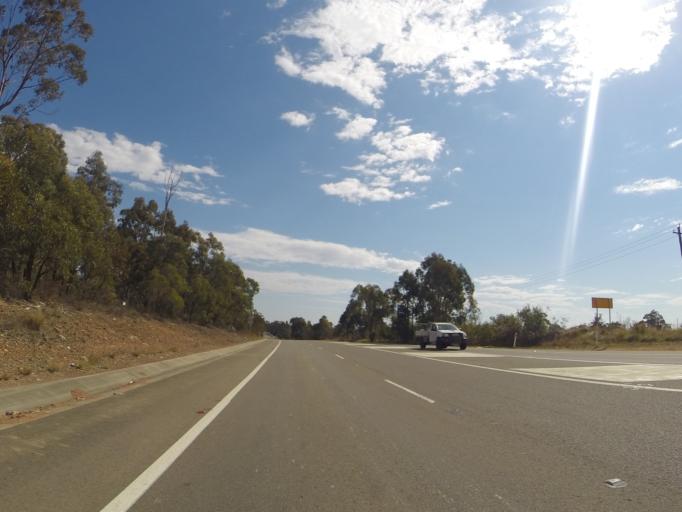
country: AU
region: New South Wales
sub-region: Liverpool
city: East Hills
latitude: -33.9732
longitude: 150.9830
